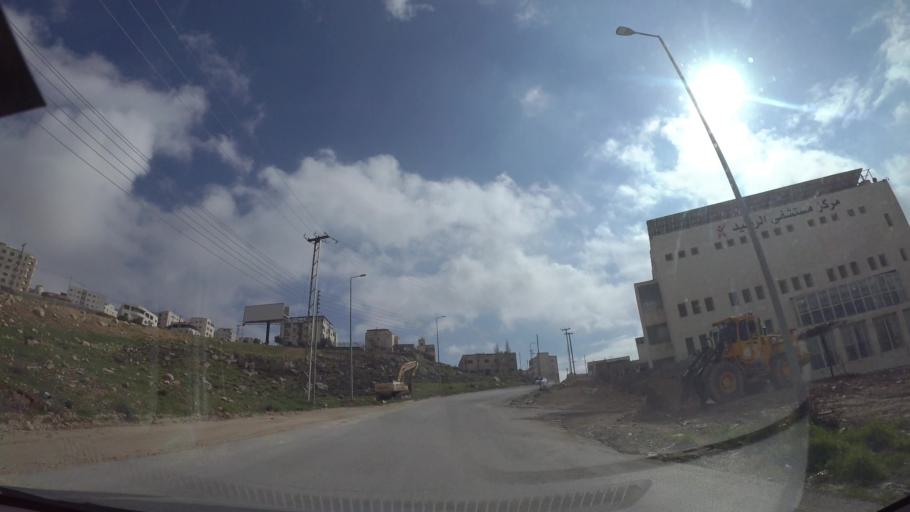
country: JO
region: Amman
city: Al Jubayhah
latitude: 32.0641
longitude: 35.8686
